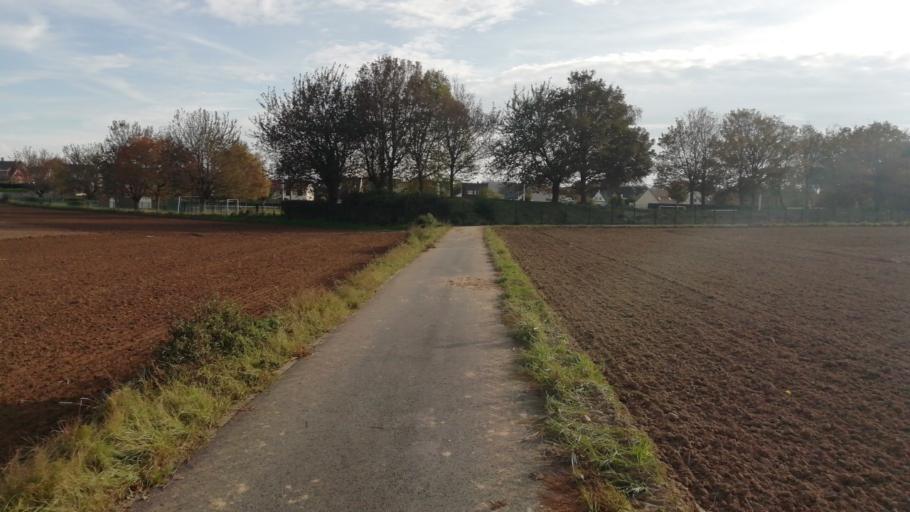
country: FR
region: Haute-Normandie
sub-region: Departement de la Seine-Maritime
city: Rogerville
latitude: 49.5082
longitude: 0.2641
